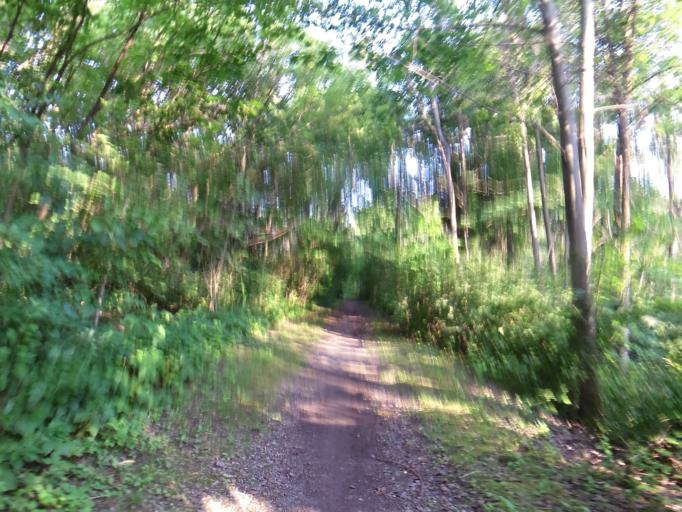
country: CA
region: Ontario
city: Bells Corners
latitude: 45.4097
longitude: -75.8813
